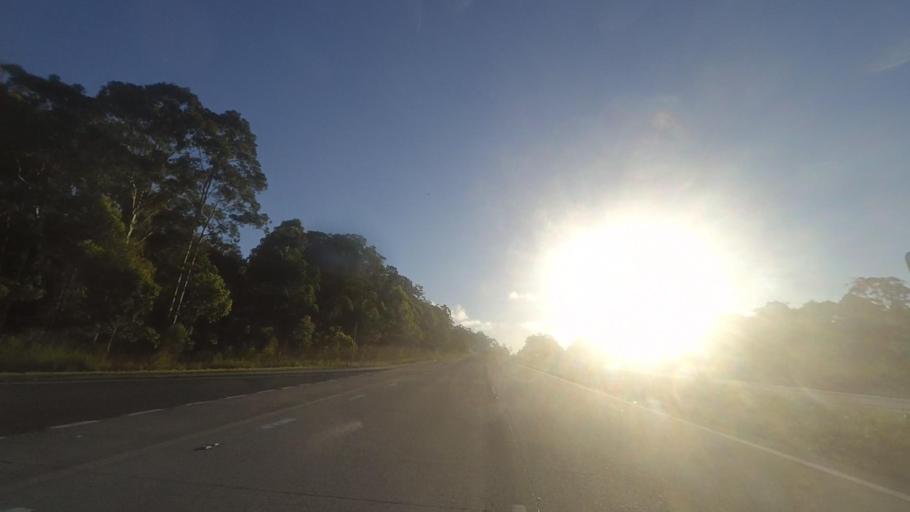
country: AU
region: New South Wales
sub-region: Great Lakes
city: Bulahdelah
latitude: -32.5323
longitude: 152.1829
